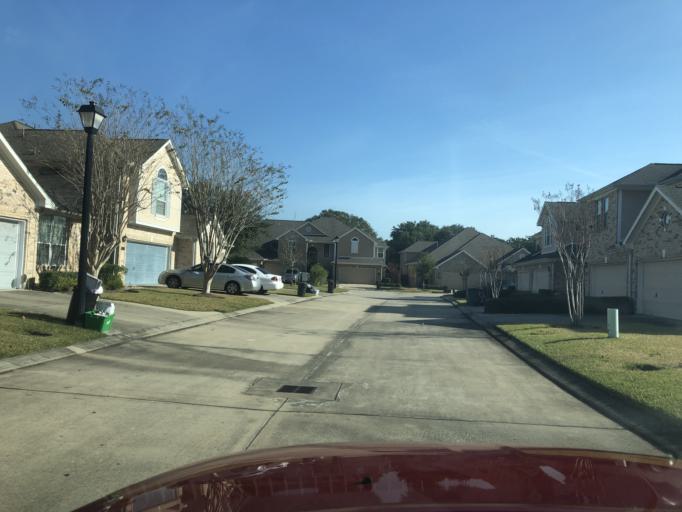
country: US
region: Texas
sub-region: Harris County
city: Spring
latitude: 30.0121
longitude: -95.4623
